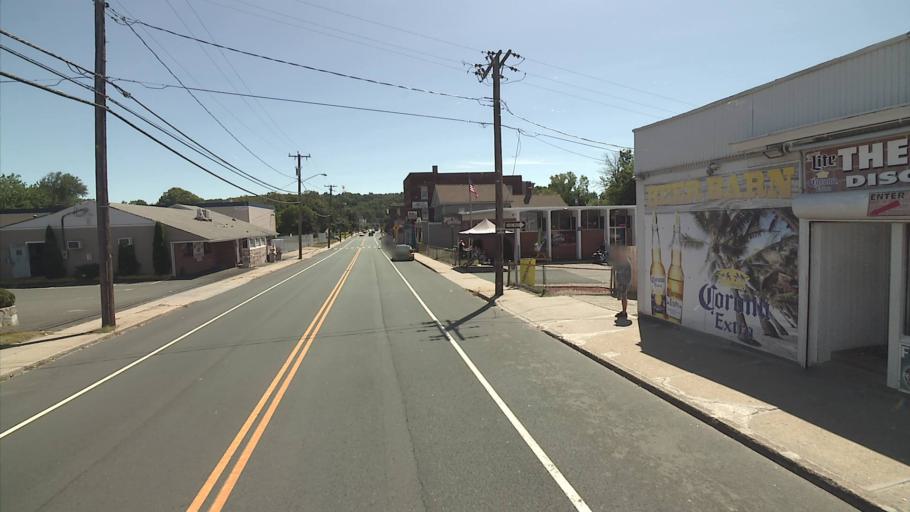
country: US
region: Connecticut
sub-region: New Haven County
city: Waterbury
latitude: 41.5899
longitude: -73.0522
